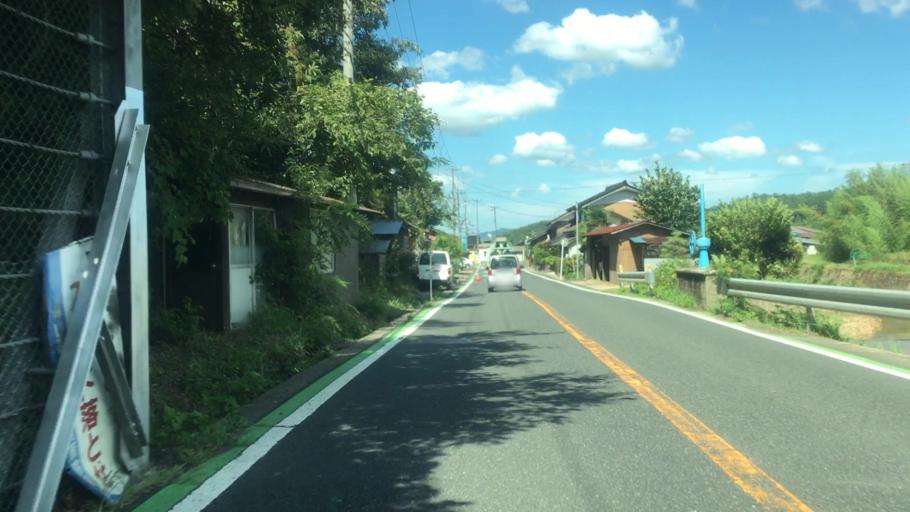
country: JP
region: Kyoto
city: Miyazu
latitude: 35.5860
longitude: 135.0357
